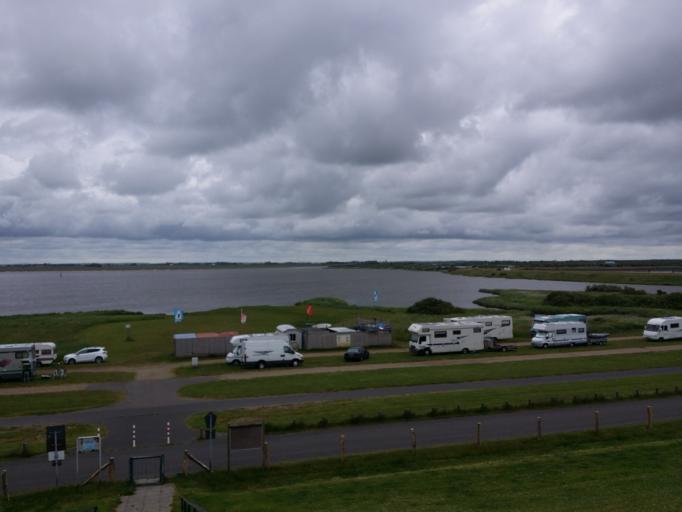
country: DE
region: Schleswig-Holstein
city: Friedrichsgabekoog
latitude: 54.0950
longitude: 8.9492
